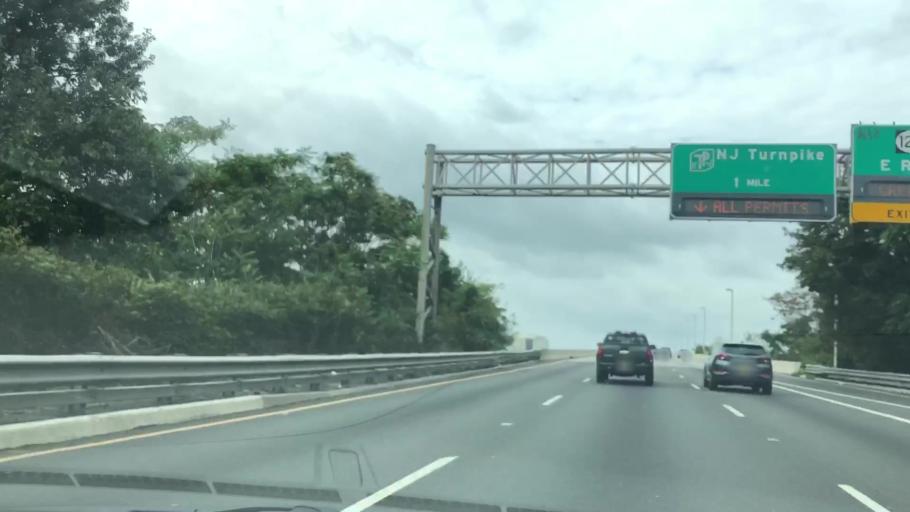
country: US
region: New Jersey
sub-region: Hudson County
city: Secaucus
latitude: 40.7981
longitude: -74.0635
